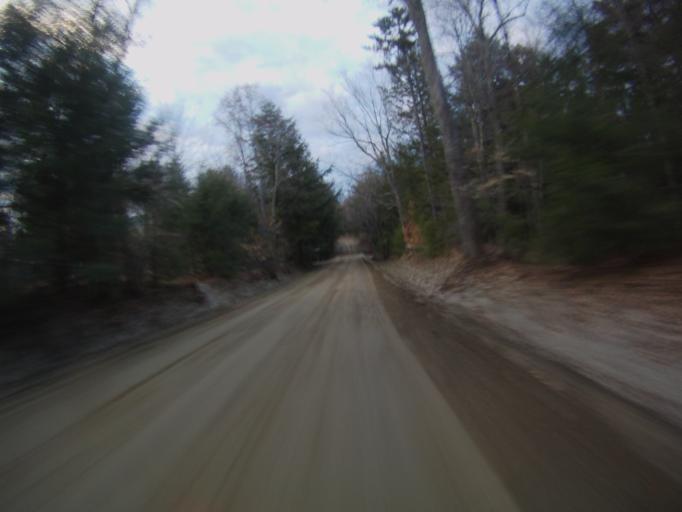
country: US
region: Vermont
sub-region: Rutland County
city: Brandon
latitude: 43.9412
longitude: -73.0222
